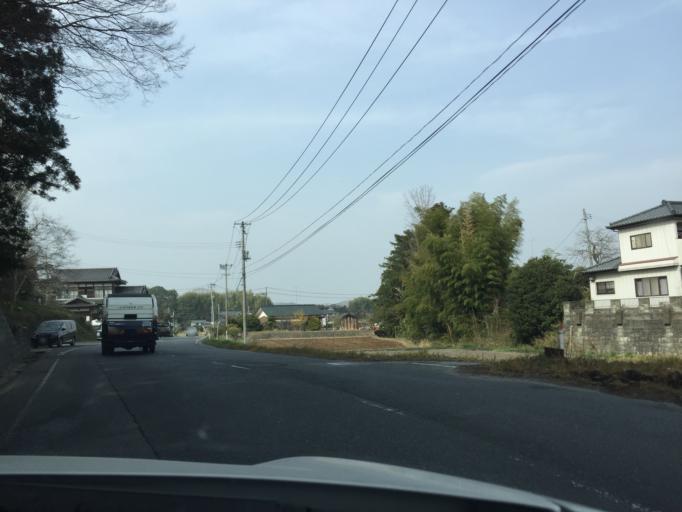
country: JP
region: Fukushima
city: Iwaki
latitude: 36.9772
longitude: 140.8560
